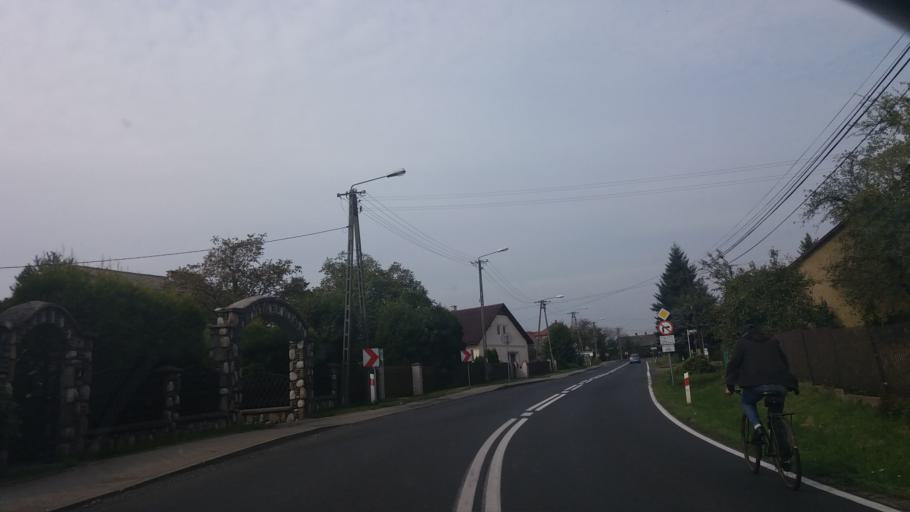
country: PL
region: Lesser Poland Voivodeship
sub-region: Powiat chrzanowski
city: Babice
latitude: 50.0664
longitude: 19.4502
